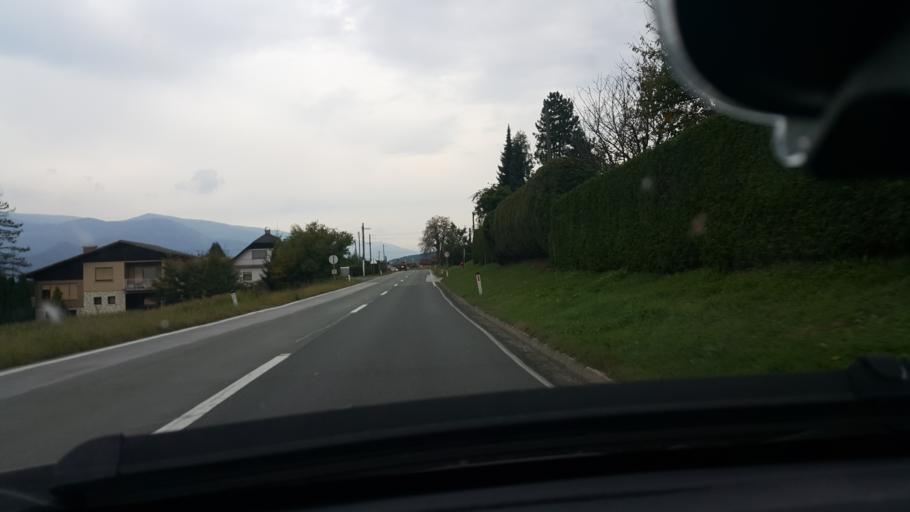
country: SI
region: Ruse
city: Ruse
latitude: 46.5585
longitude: 15.5213
